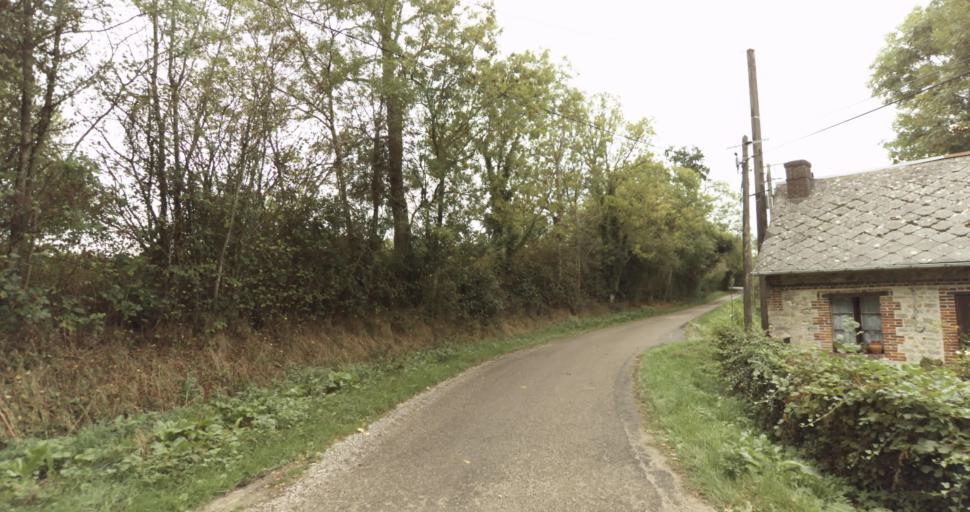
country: FR
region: Lower Normandy
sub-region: Departement de l'Orne
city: Sainte-Gauburge-Sainte-Colombe
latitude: 48.7617
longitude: 0.3795
